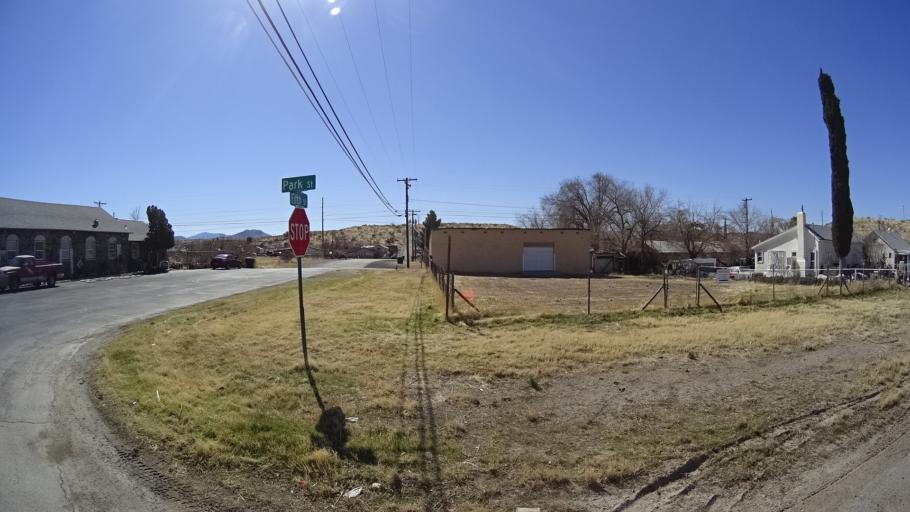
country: US
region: Arizona
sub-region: Mohave County
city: Kingman
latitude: 35.1866
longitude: -114.0518
